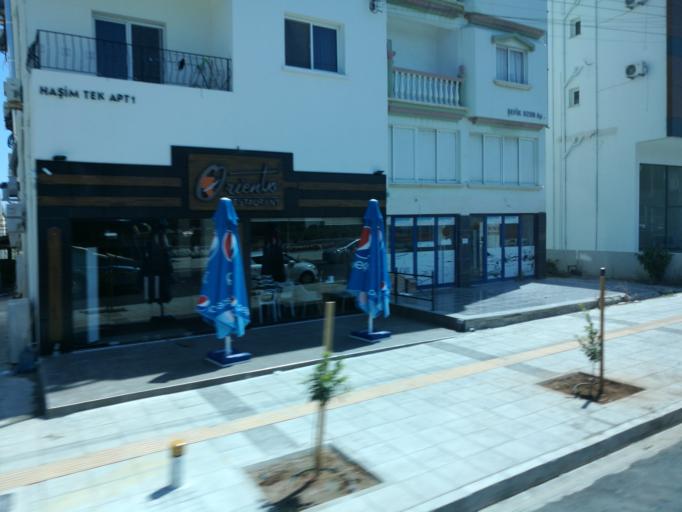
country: CY
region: Ammochostos
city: Famagusta
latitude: 35.1441
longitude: 33.9129
